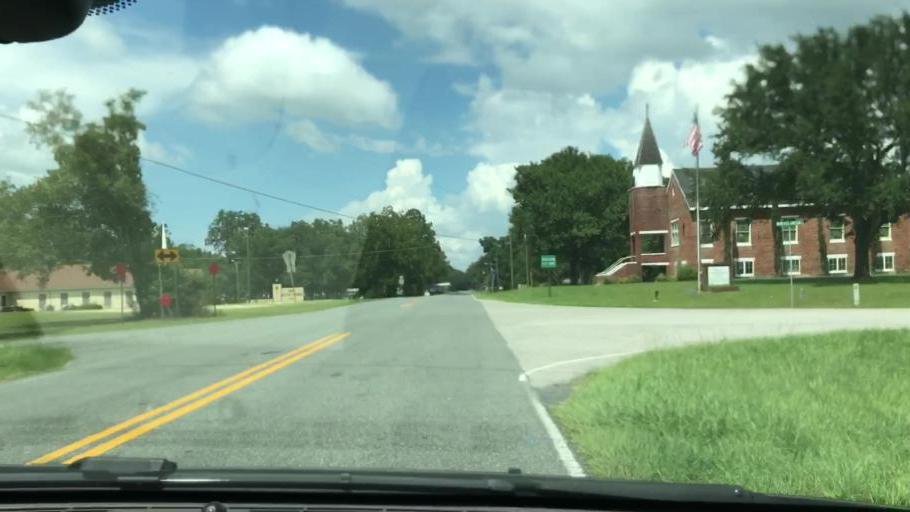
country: US
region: Florida
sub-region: Jackson County
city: Malone
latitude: 30.9221
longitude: -85.1187
